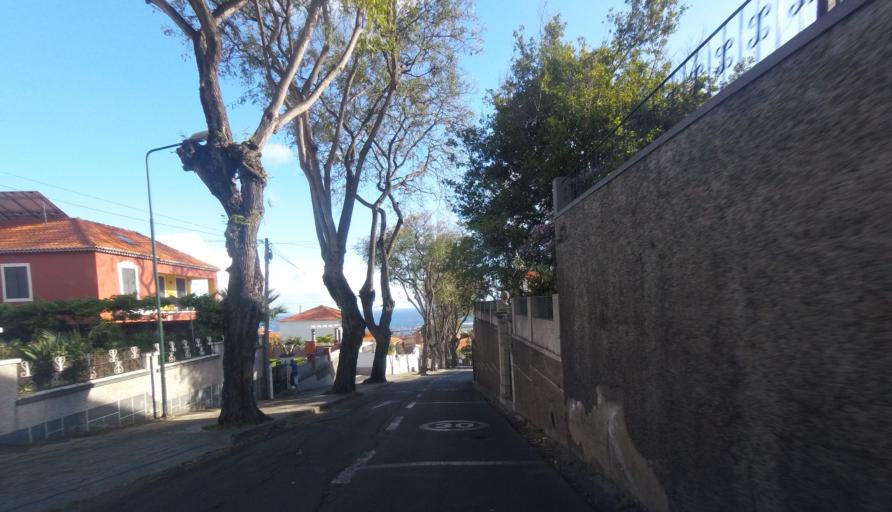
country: PT
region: Madeira
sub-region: Funchal
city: Nossa Senhora do Monte
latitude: 32.6567
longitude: -16.9042
